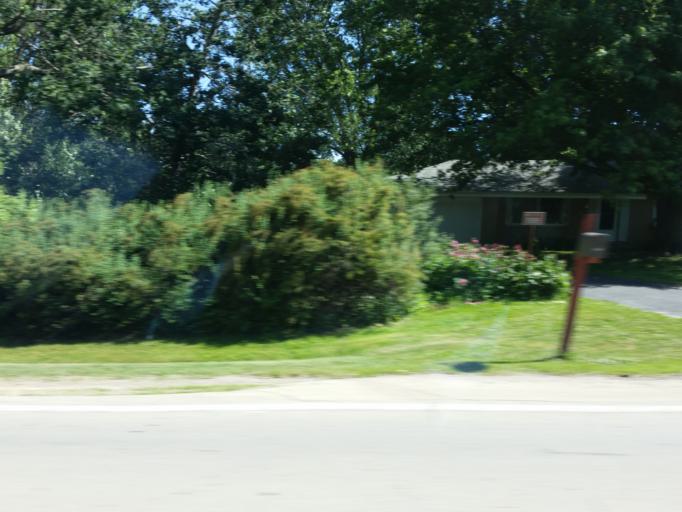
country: US
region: Illinois
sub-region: Ogle County
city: Davis Junction
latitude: 42.1005
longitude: -89.0399
